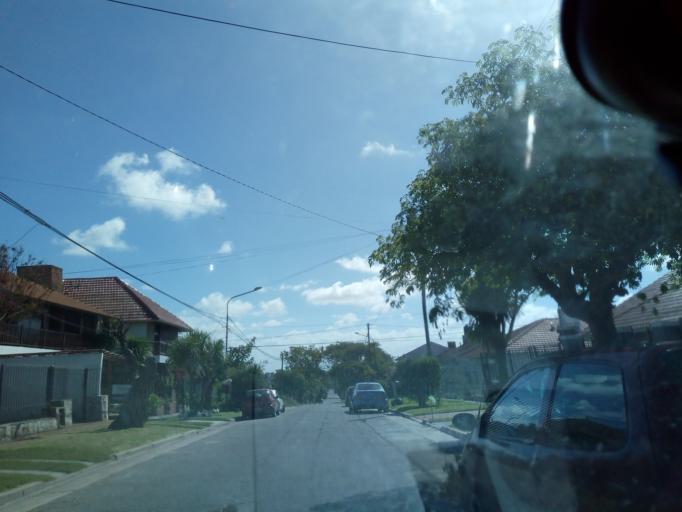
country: AR
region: Buenos Aires
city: Mar del Plata
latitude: -38.0559
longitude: -57.5515
